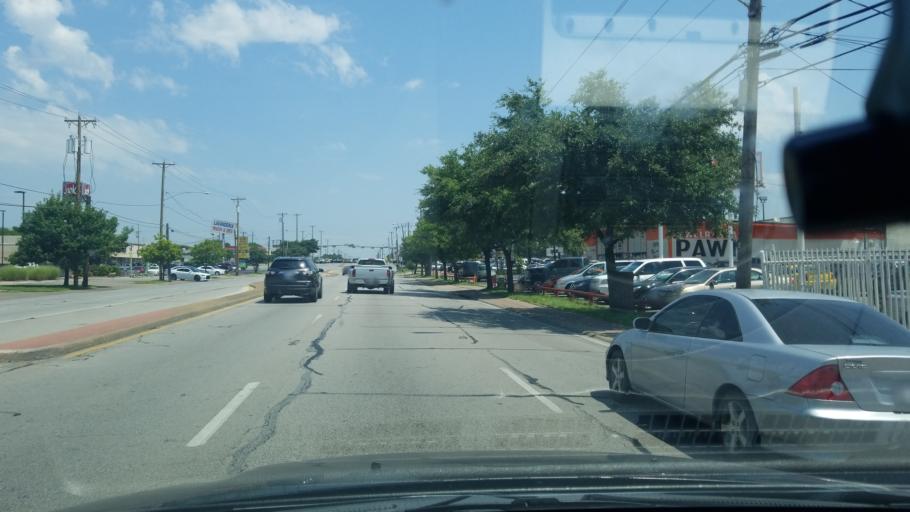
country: US
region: Texas
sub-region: Dallas County
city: Balch Springs
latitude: 32.7463
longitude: -96.6828
